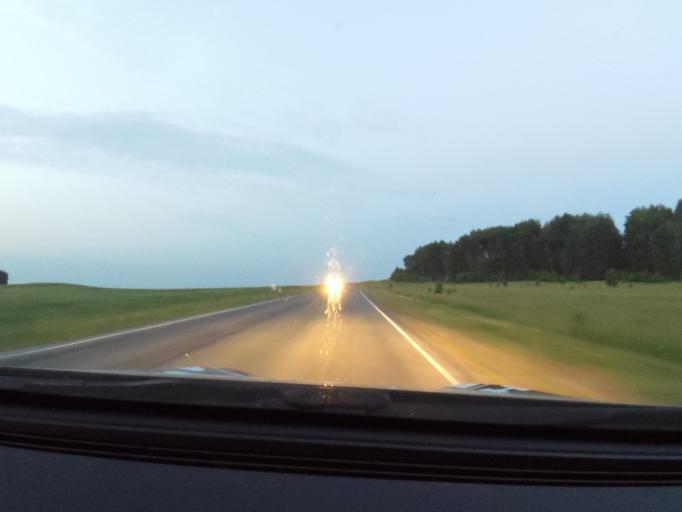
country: RU
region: Bashkortostan
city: Duvan
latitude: 56.0773
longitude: 58.1003
